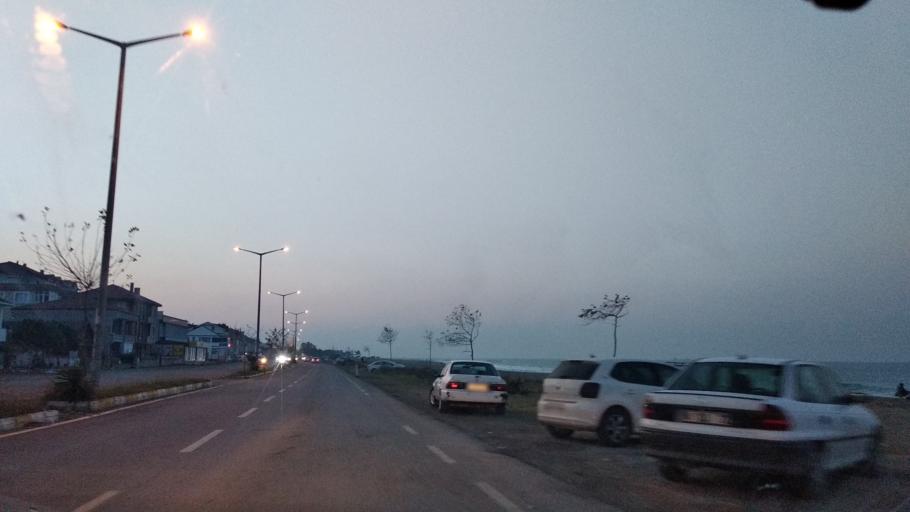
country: TR
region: Sakarya
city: Karasu
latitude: 41.0913
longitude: 30.7418
